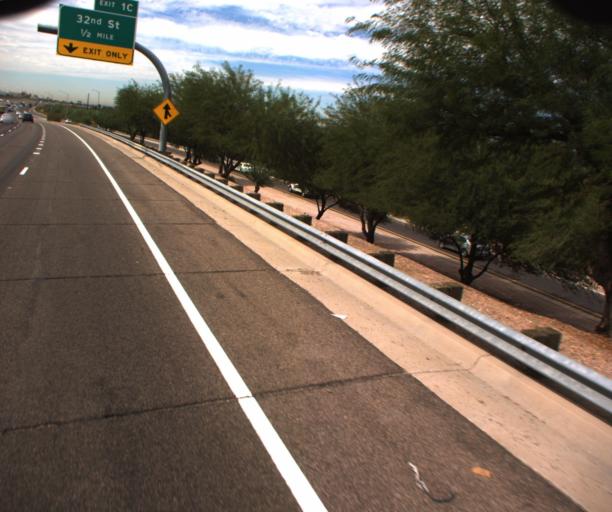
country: US
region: Arizona
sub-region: Maricopa County
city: Tempe Junction
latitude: 33.4595
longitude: -111.9974
